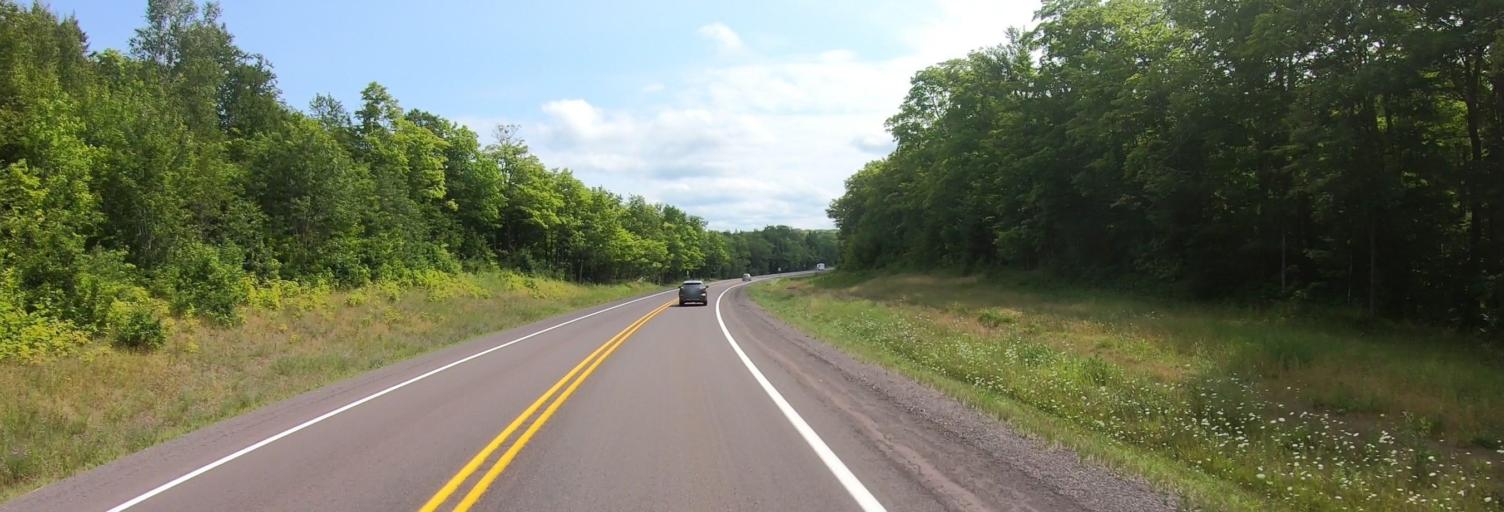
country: US
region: Michigan
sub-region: Houghton County
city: Hancock
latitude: 46.9673
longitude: -88.7771
